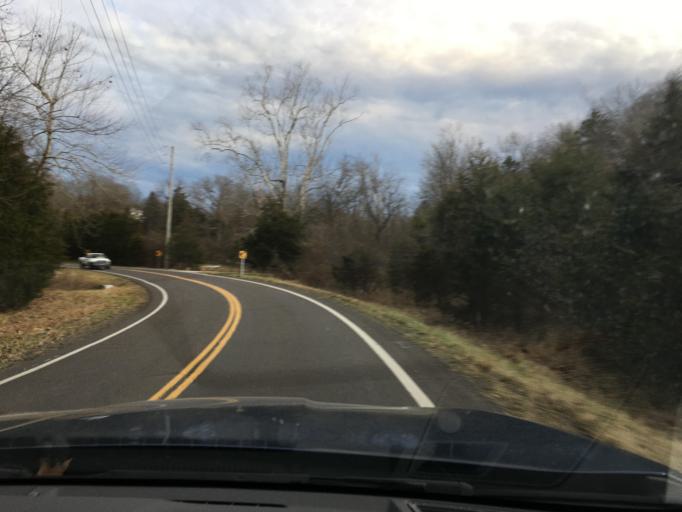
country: US
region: Missouri
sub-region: Jefferson County
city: De Soto
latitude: 38.1087
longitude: -90.5641
